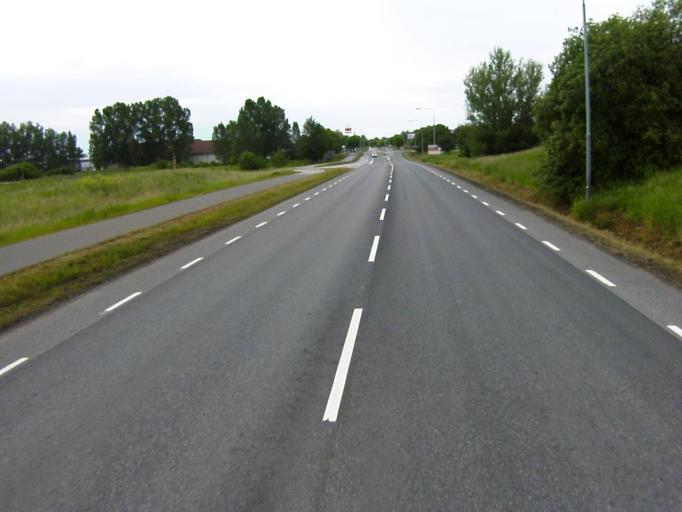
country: SE
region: Skane
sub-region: Kristianstads Kommun
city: Kristianstad
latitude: 56.0257
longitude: 14.1408
